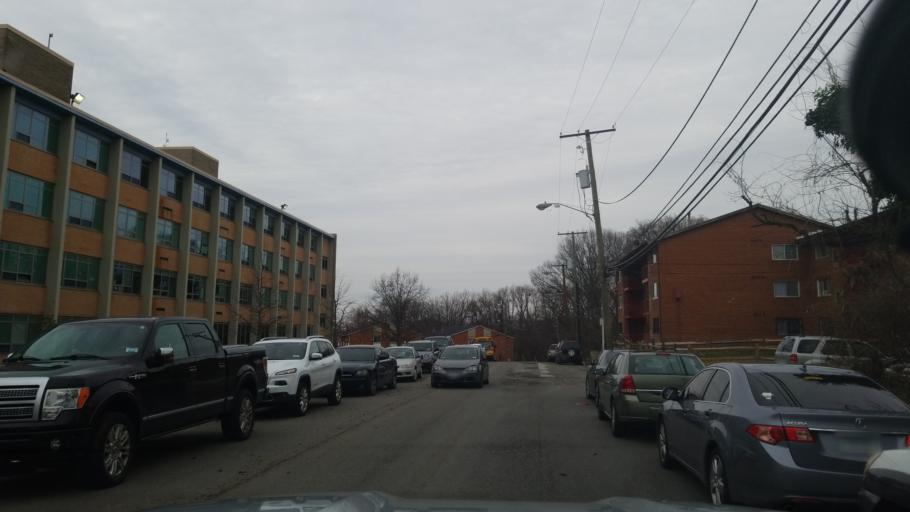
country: US
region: Maryland
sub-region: Prince George's County
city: Hillcrest Heights
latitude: 38.8514
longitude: -76.9833
